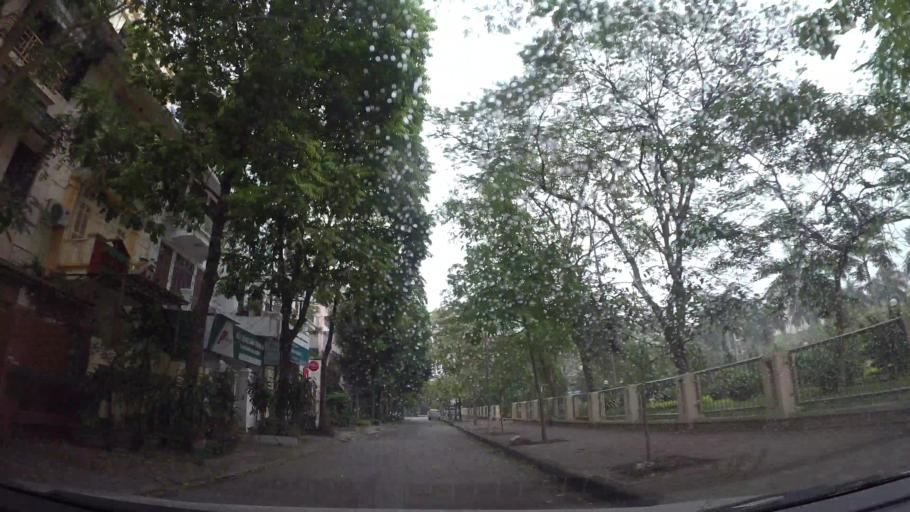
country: VN
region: Ha Noi
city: Cau Giay
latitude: 21.0155
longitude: 105.7987
